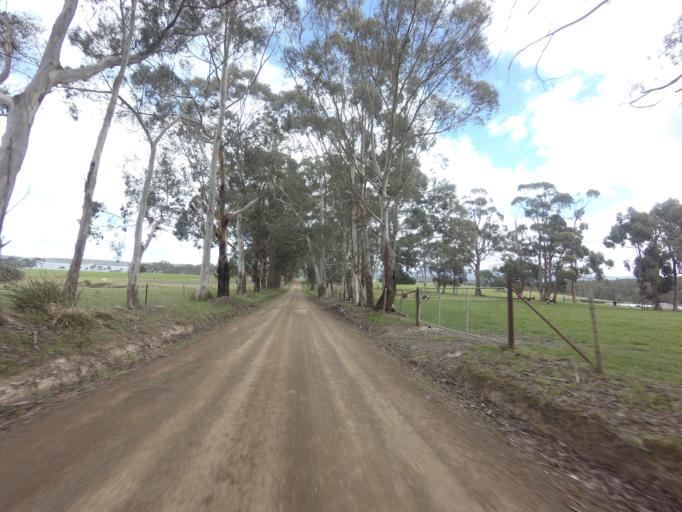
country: AU
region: Tasmania
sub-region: Huon Valley
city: Geeveston
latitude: -43.4286
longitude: 146.9932
